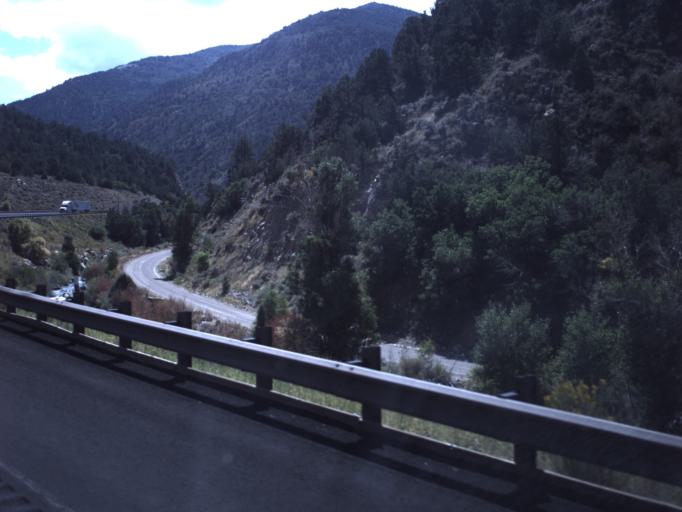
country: US
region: Utah
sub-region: Sevier County
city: Salina
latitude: 38.9043
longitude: -111.6351
